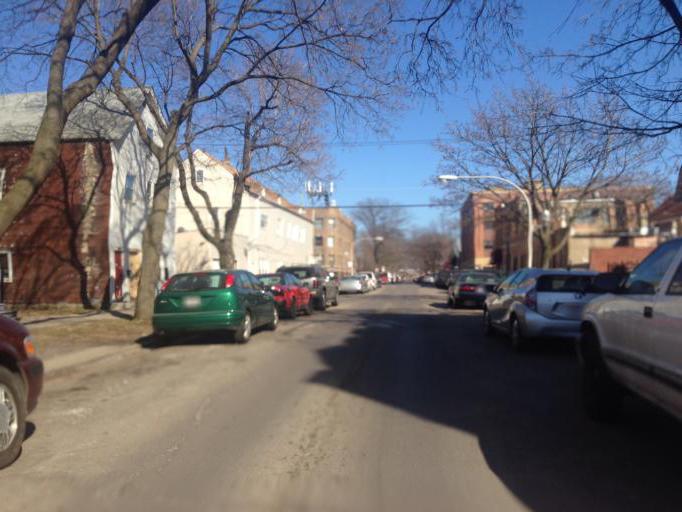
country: US
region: Illinois
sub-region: Cook County
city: Lincolnwood
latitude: 41.9366
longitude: -87.6988
